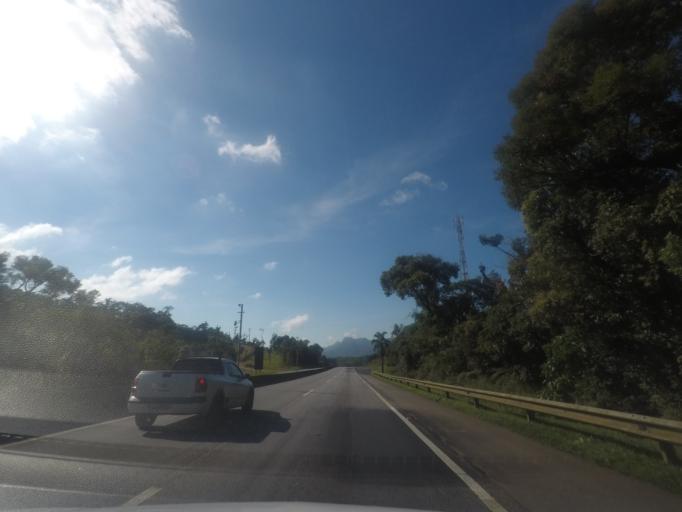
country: BR
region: Parana
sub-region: Piraquara
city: Piraquara
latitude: -25.5865
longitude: -48.9532
